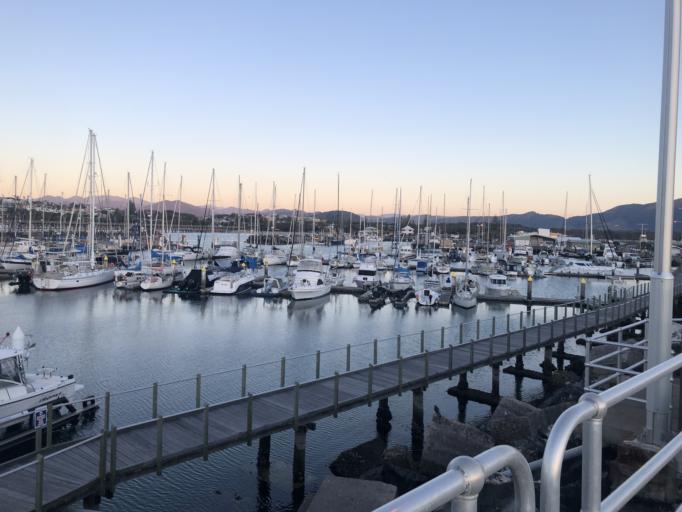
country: AU
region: New South Wales
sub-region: Coffs Harbour
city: Coffs Harbour
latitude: -30.3040
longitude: 153.1478
